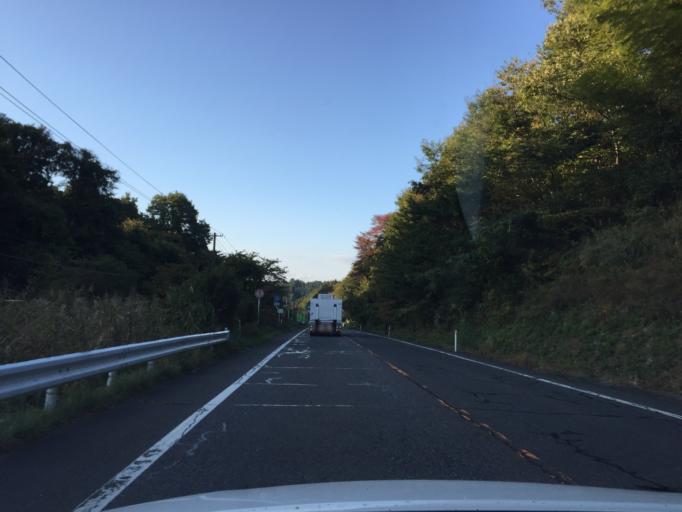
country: JP
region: Fukushima
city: Ishikawa
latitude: 37.2047
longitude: 140.6101
